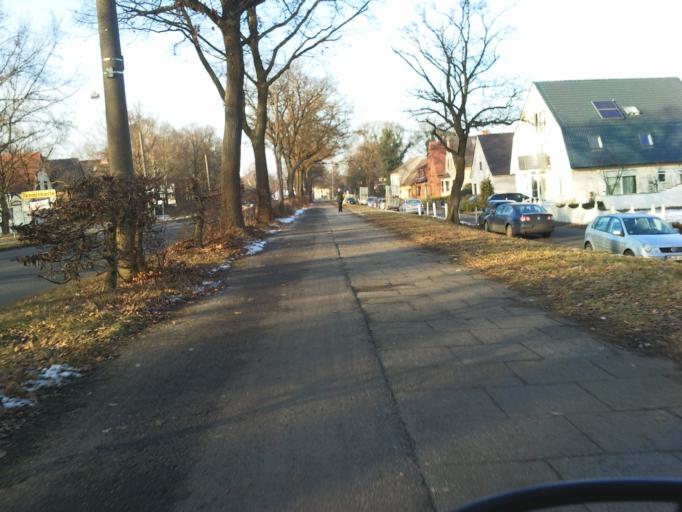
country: DE
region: Lower Saxony
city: Ritterhude
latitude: 53.1479
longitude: 8.7113
